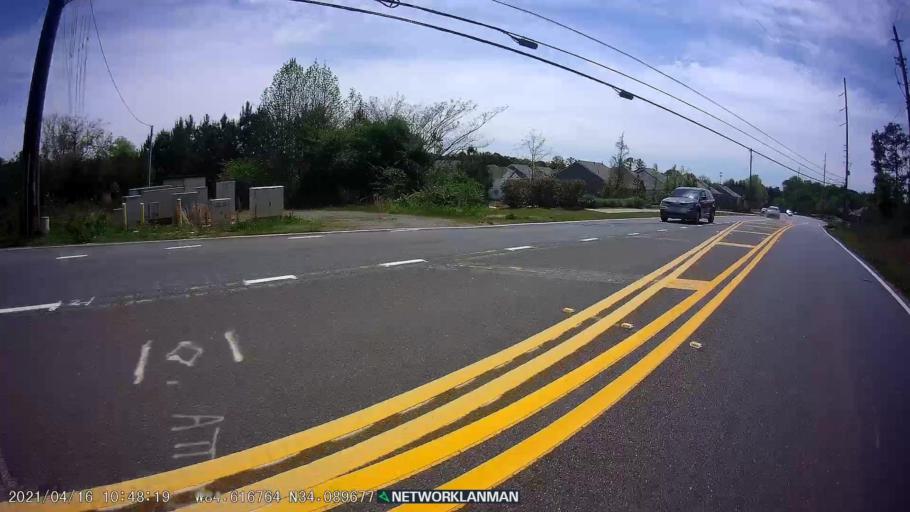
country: US
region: Georgia
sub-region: Cobb County
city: Acworth
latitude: 34.0896
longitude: -84.6167
